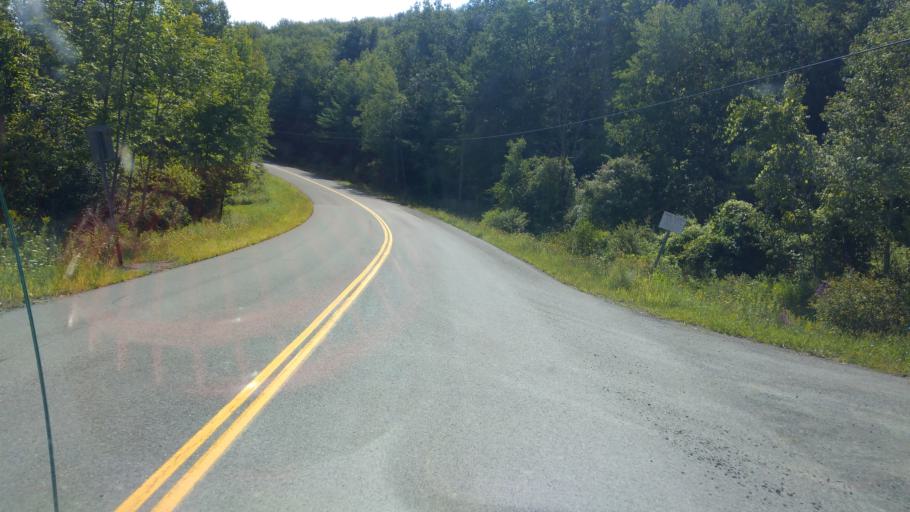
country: US
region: New York
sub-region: Allegany County
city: Belmont
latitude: 42.2914
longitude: -78.0018
